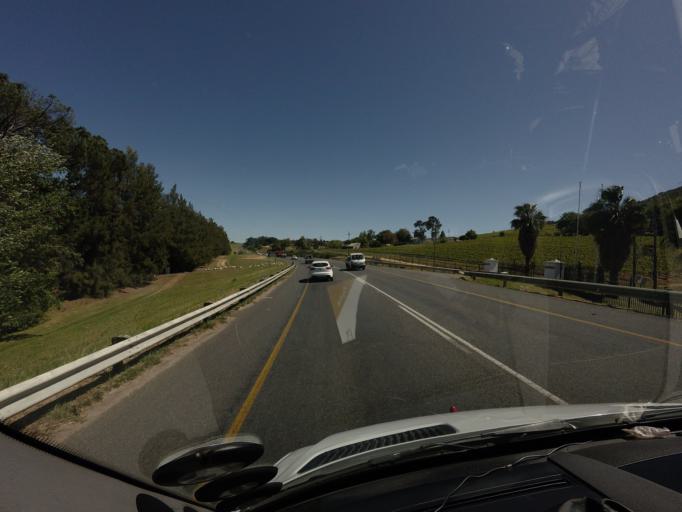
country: ZA
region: Western Cape
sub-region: Cape Winelands District Municipality
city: Stellenbosch
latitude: -33.8928
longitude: 18.8581
